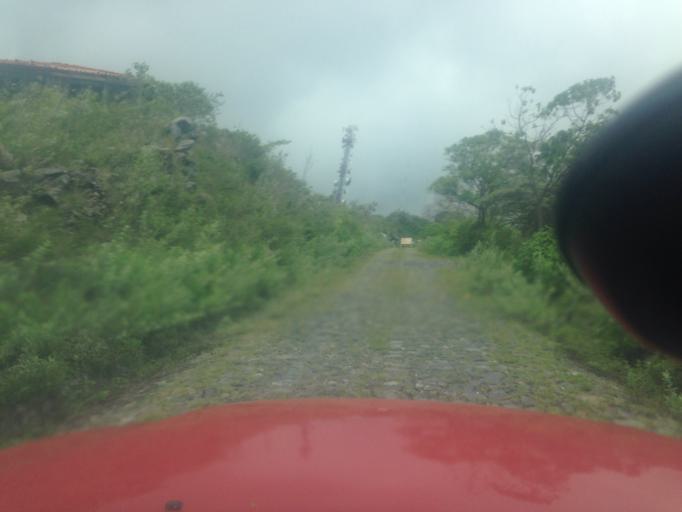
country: MX
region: Nayarit
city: Jala
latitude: 21.1336
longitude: -104.5018
